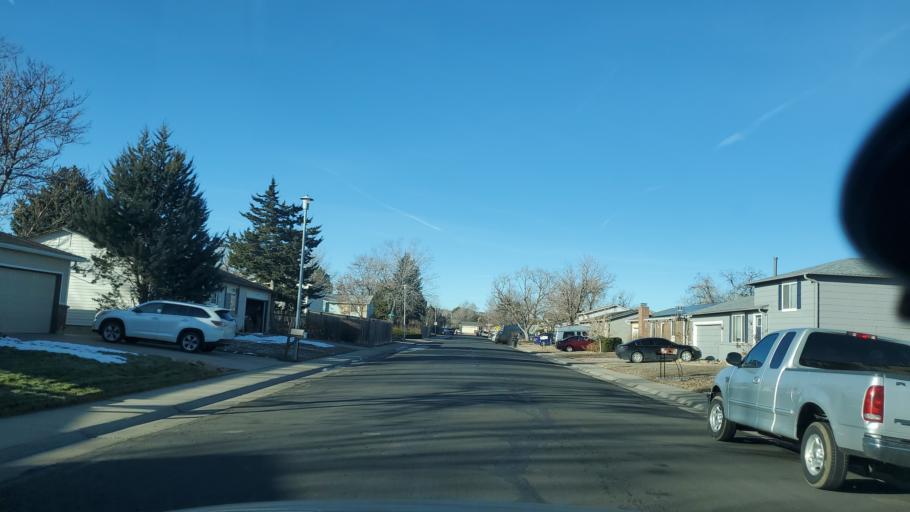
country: US
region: Colorado
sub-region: Adams County
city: Northglenn
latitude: 39.9133
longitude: -104.9463
